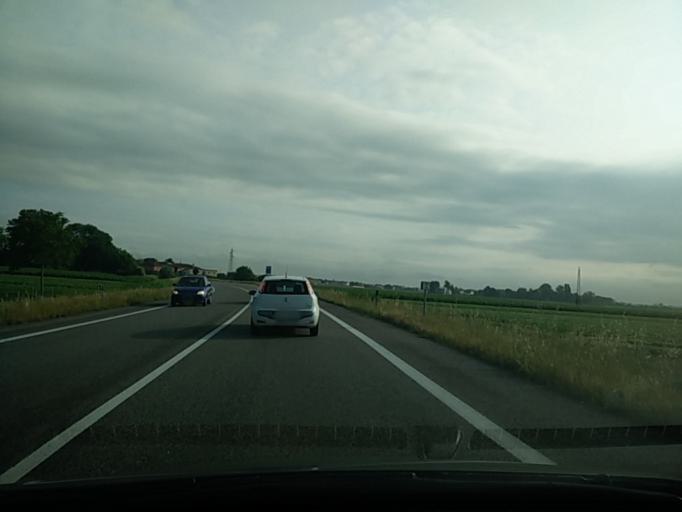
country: IT
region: Veneto
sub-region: Provincia di Venezia
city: San Dona di Piave
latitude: 45.6267
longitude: 12.6024
